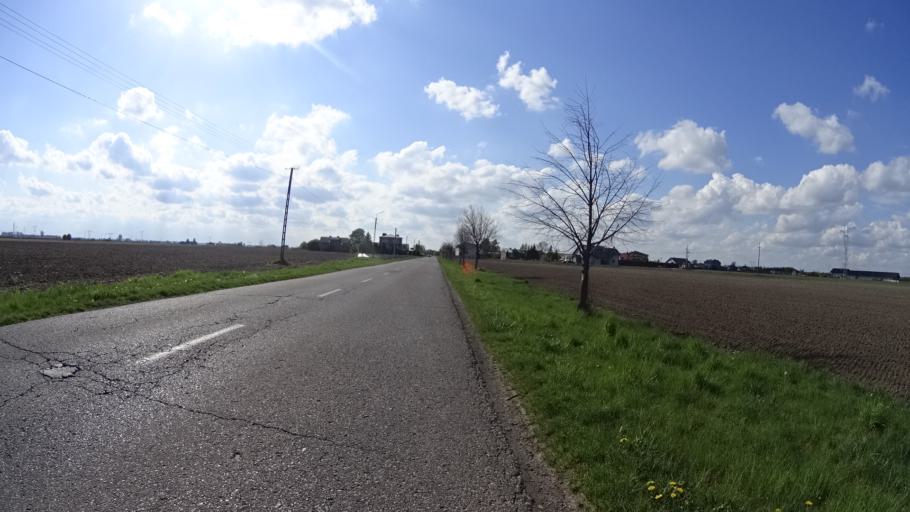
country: PL
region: Masovian Voivodeship
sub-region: Powiat warszawski zachodni
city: Jozefow
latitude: 52.2337
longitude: 20.6800
